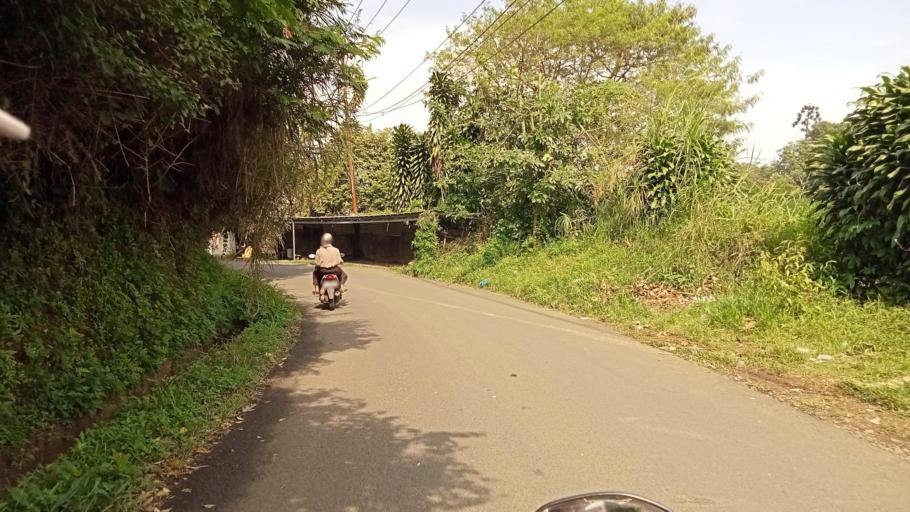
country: ID
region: West Java
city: Caringin
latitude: -6.6478
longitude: 106.9089
